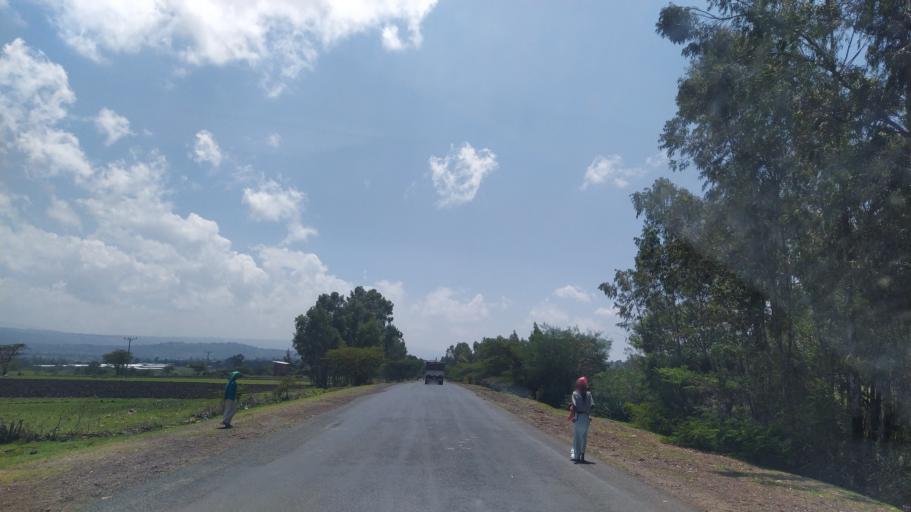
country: ET
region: Southern Nations, Nationalities, and People's Region
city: Butajira
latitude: 7.7646
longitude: 38.1351
